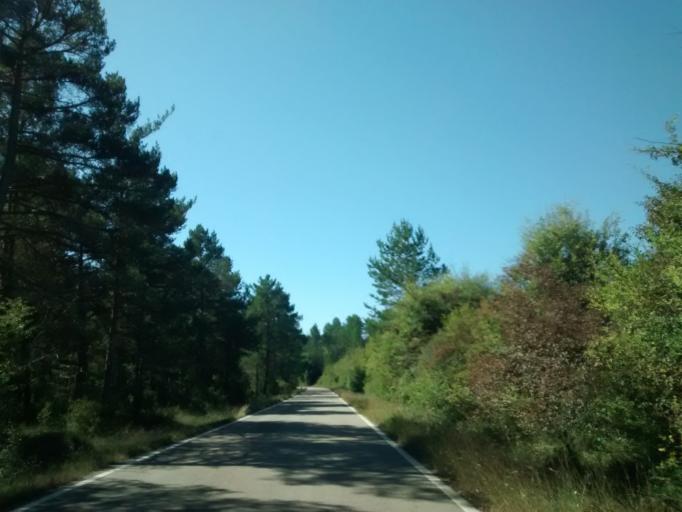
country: ES
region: Aragon
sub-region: Provincia de Huesca
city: Santa Cruz de la Seros
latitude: 42.4336
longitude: -0.6220
